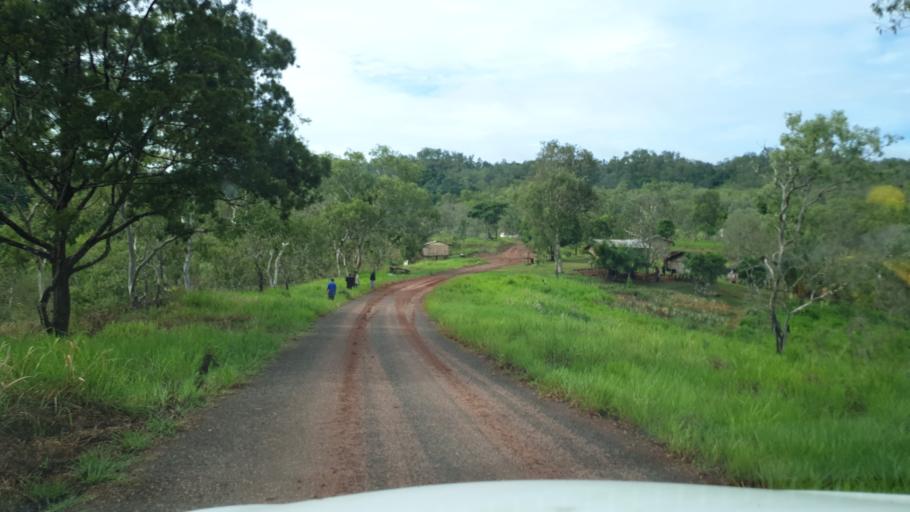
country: PG
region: National Capital
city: Port Moresby
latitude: -9.4345
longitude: 147.3967
